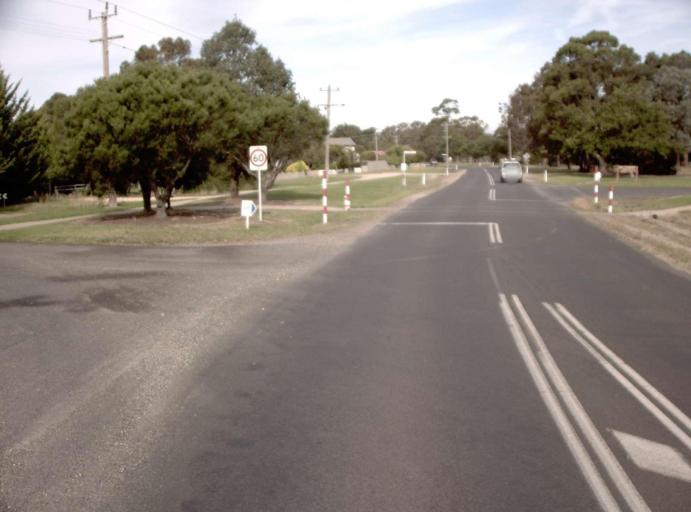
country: AU
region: Victoria
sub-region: Latrobe
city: Traralgon
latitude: -38.0600
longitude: 146.6258
